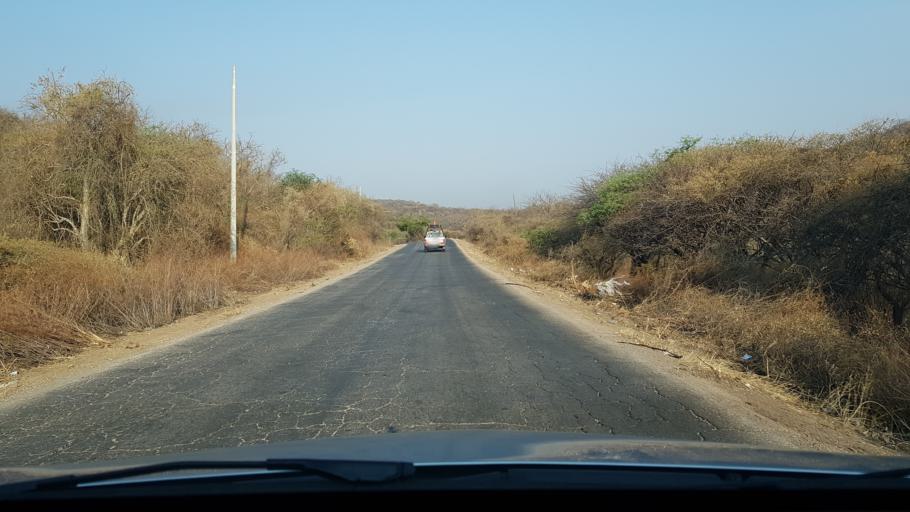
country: MX
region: Morelos
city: Tlaltizapan
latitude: 18.6757
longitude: -99.0712
